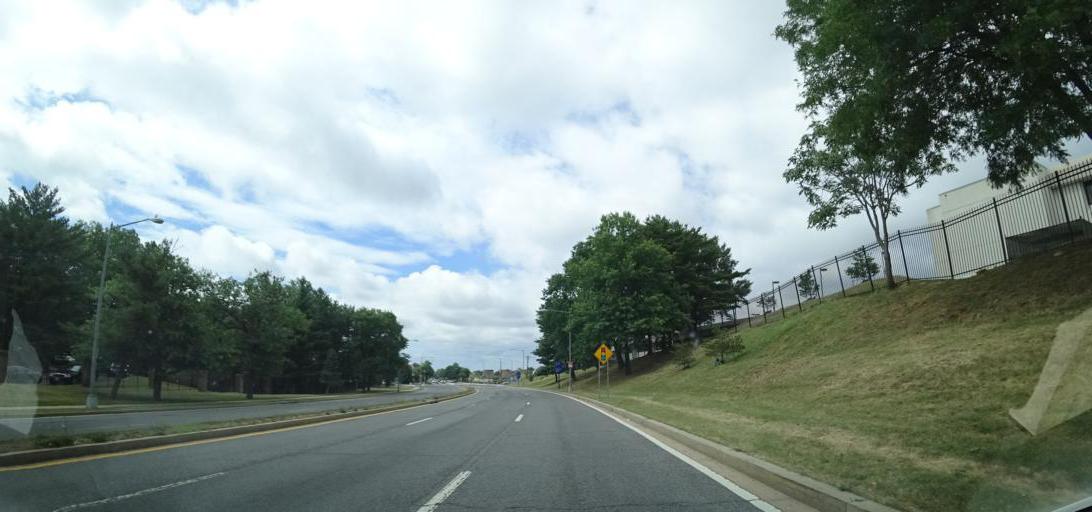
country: US
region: Maryland
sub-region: Prince George's County
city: Chillum
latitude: 38.9282
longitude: -77.0089
